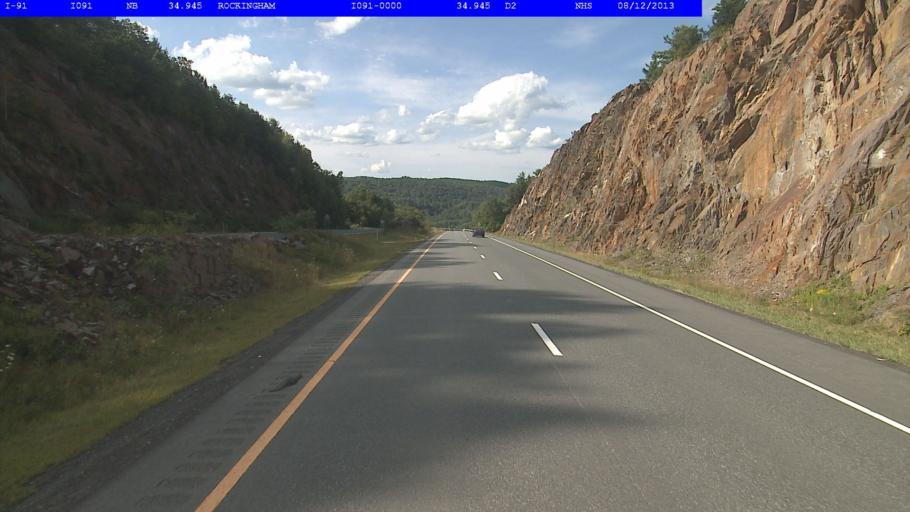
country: US
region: Vermont
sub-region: Windham County
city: Rockingham
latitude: 43.1750
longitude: -72.4627
